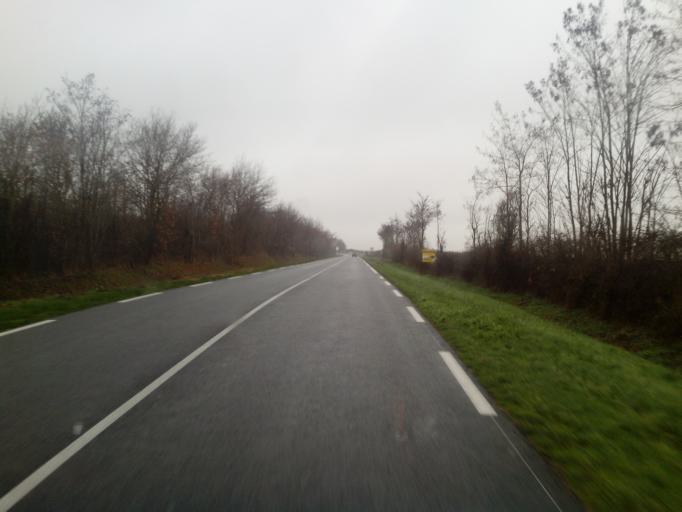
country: FR
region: Poitou-Charentes
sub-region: Departement de la Vienne
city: Terce
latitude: 46.4526
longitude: 0.5649
